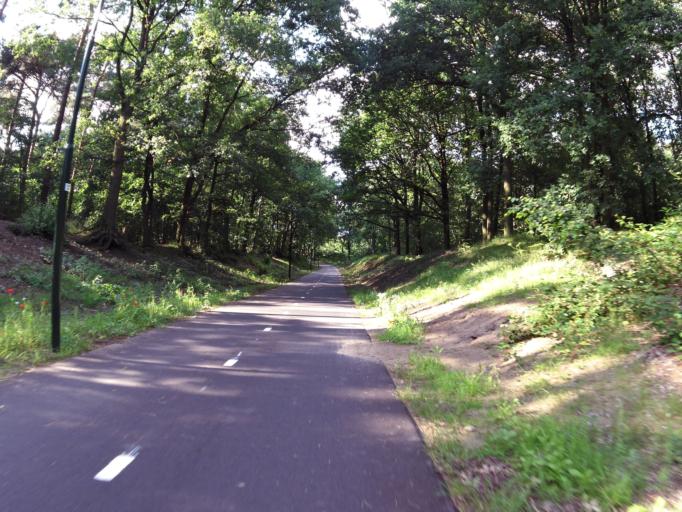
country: NL
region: North Brabant
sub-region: Gemeente Waalre
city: Waalre
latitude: 51.3999
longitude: 5.4615
